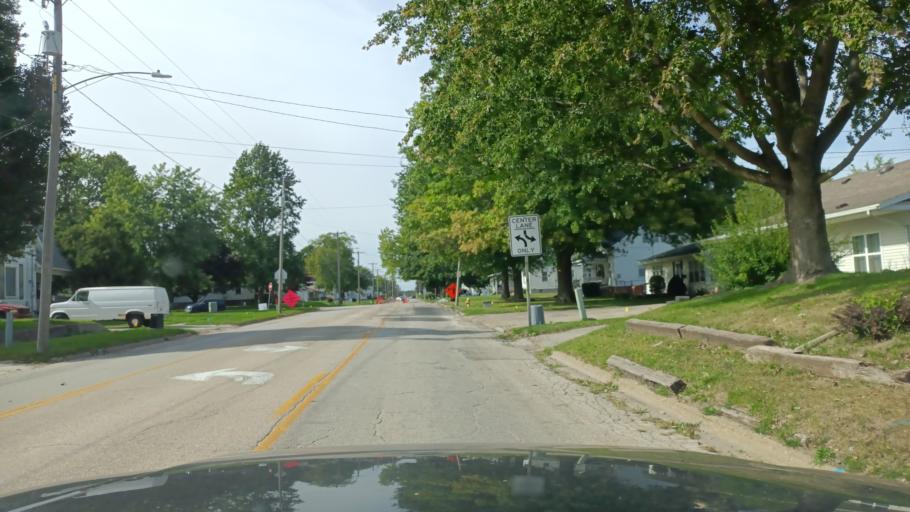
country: US
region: Illinois
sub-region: Knox County
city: Galesburg
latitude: 40.9416
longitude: -90.3463
